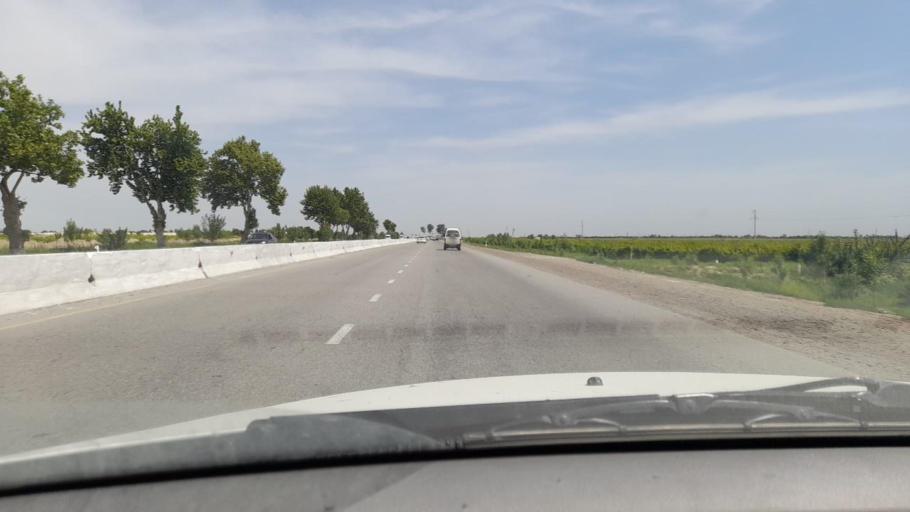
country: UZ
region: Bukhara
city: Galaosiyo
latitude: 39.8947
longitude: 64.4689
